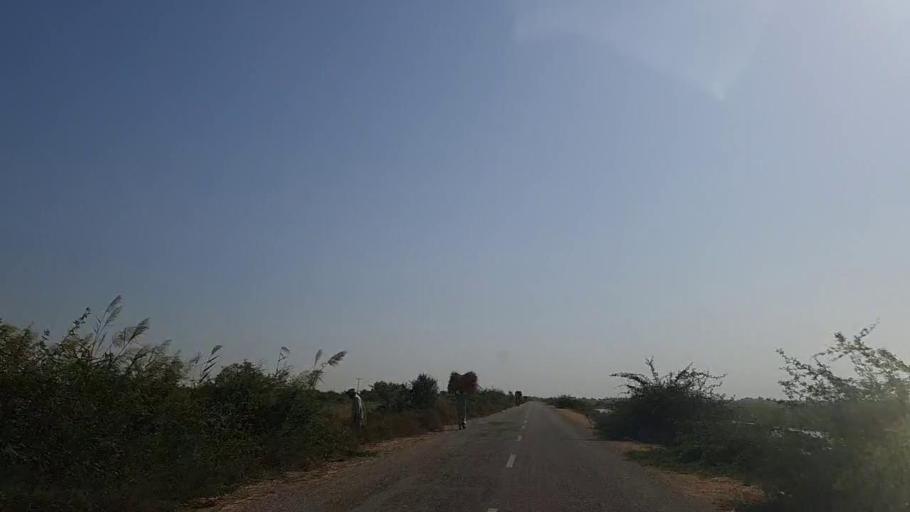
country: PK
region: Sindh
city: Jati
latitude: 24.5032
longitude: 68.2745
